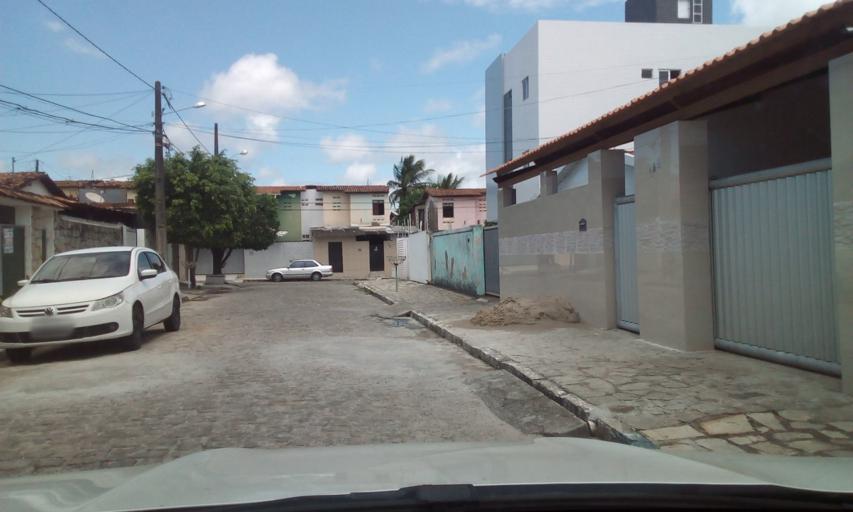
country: BR
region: Paraiba
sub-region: Joao Pessoa
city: Joao Pessoa
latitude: -7.1773
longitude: -34.8416
